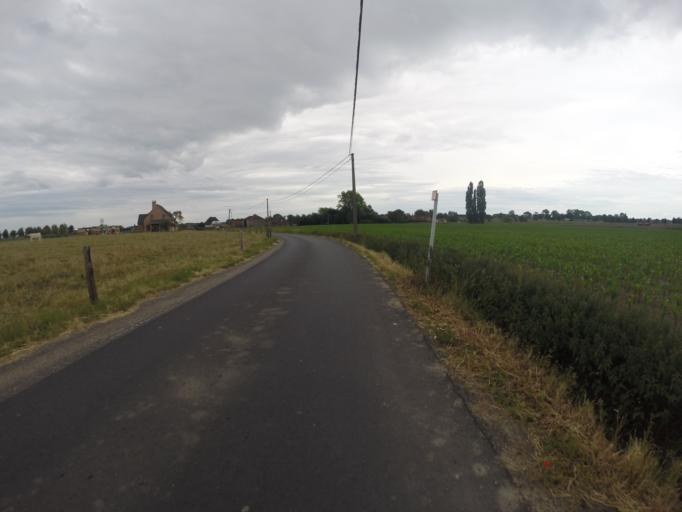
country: BE
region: Flanders
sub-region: Provincie West-Vlaanderen
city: Ruiselede
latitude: 51.0408
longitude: 3.3653
